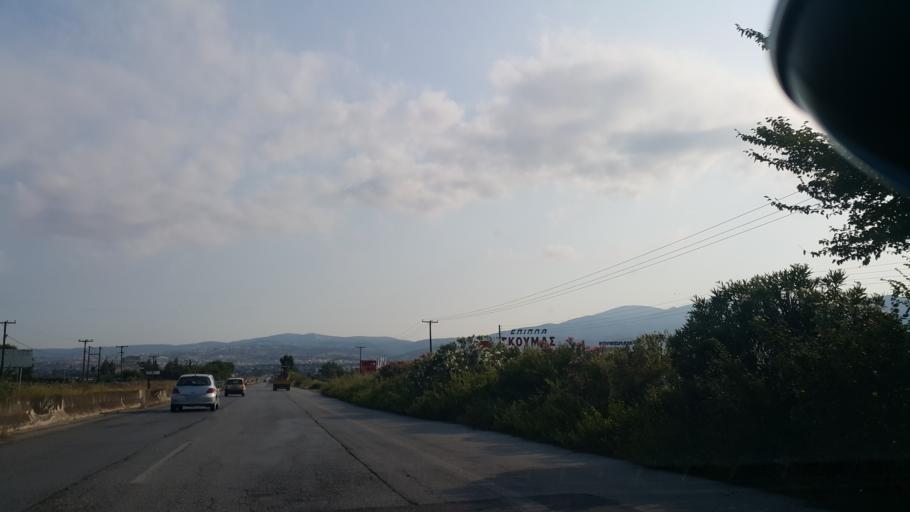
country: GR
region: Central Macedonia
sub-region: Nomos Thessalonikis
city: Neo Rysi
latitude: 40.5032
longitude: 23.0058
